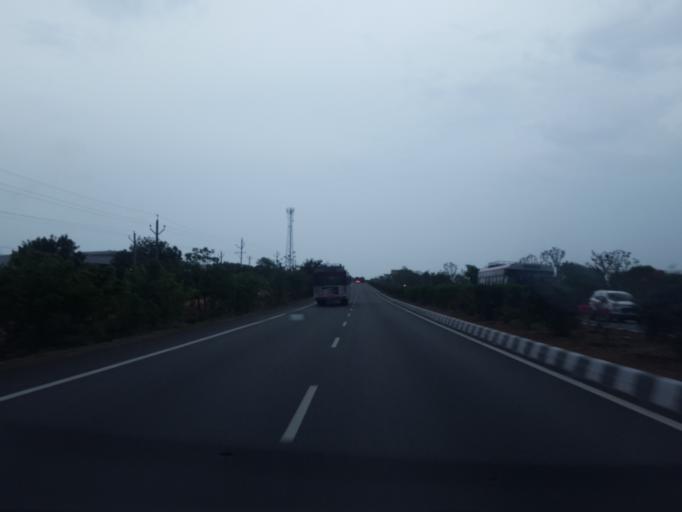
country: IN
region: Telangana
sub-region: Mahbubnagar
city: Farrukhnagar
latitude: 17.1084
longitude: 78.2598
